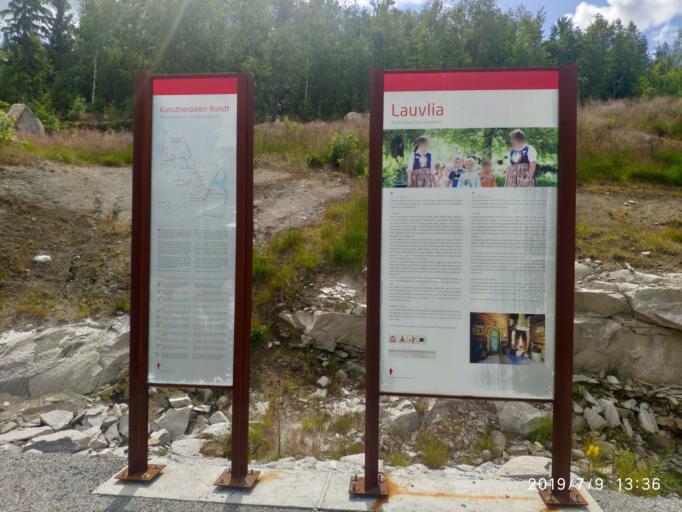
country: NO
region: Buskerud
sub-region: Sigdal
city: Prestfoss
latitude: 60.0611
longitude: 9.5076
